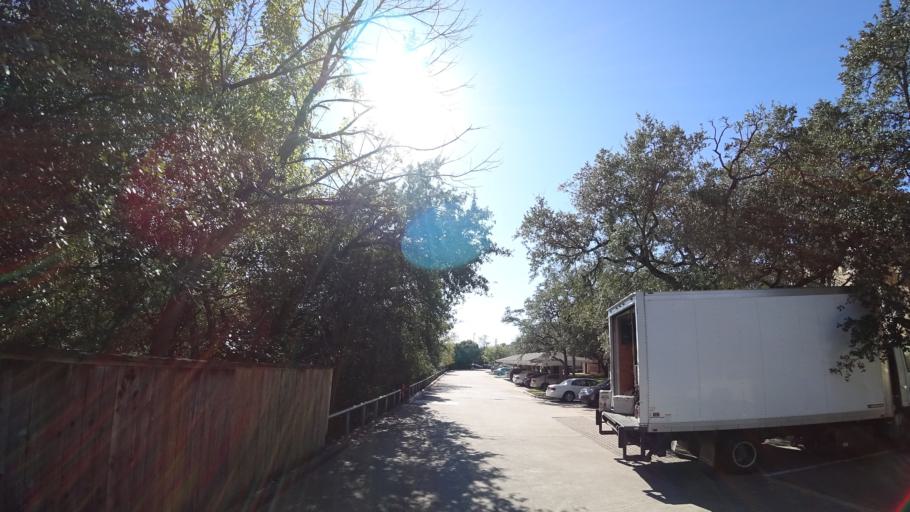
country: US
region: Texas
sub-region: Williamson County
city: Jollyville
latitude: 30.4123
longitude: -97.7512
